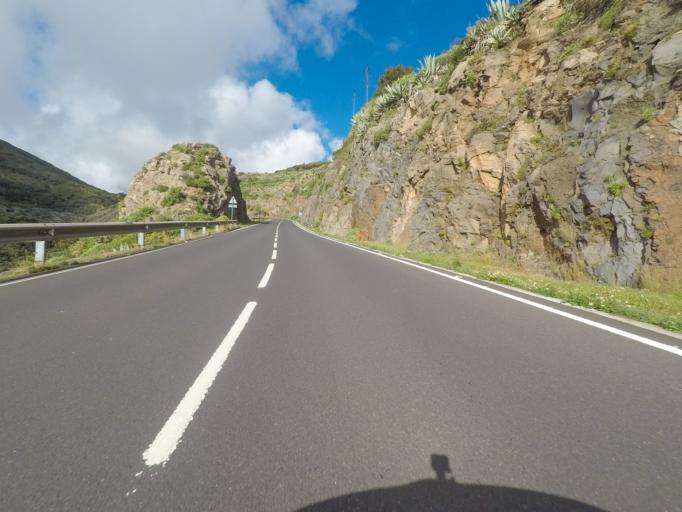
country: ES
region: Canary Islands
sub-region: Provincia de Santa Cruz de Tenerife
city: Alajero
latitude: 28.0994
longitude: -17.1896
